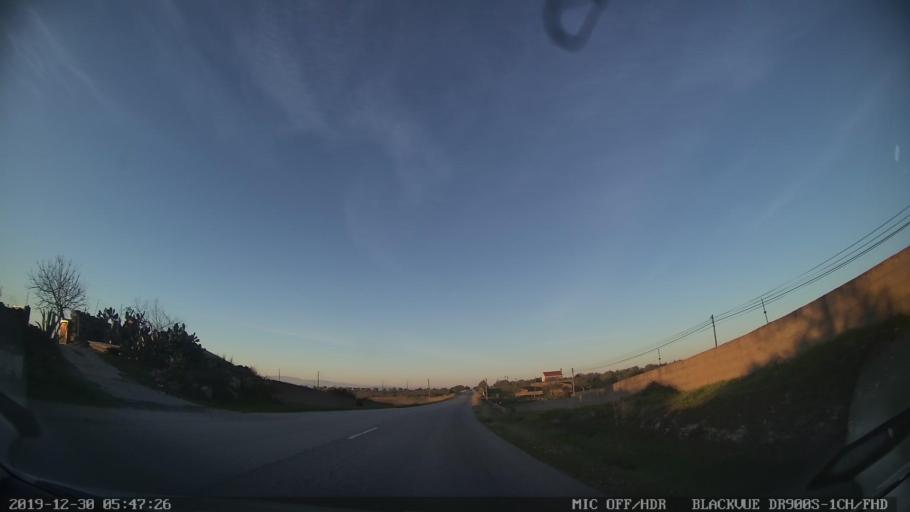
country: PT
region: Castelo Branco
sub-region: Idanha-A-Nova
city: Idanha-a-Nova
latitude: 39.9505
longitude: -7.2397
